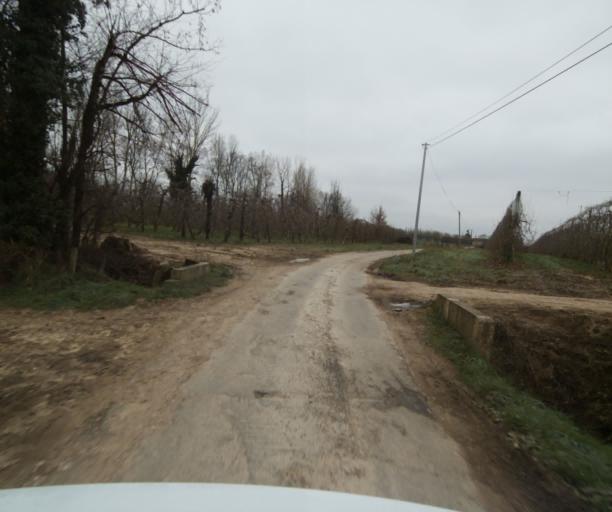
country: FR
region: Midi-Pyrenees
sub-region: Departement du Tarn-et-Garonne
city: Moissac
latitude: 44.1162
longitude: 1.1462
